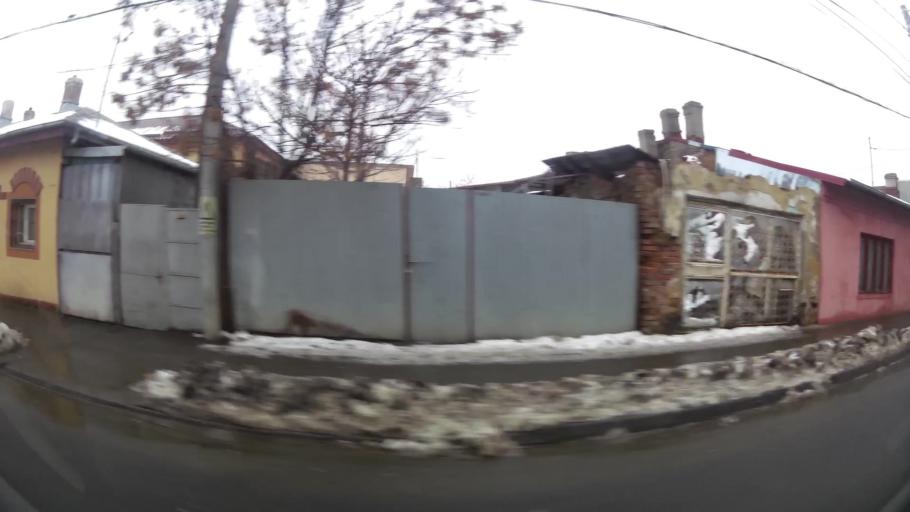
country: RO
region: Ilfov
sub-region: Comuna Chiajna
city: Rosu
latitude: 44.4665
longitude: 26.0345
